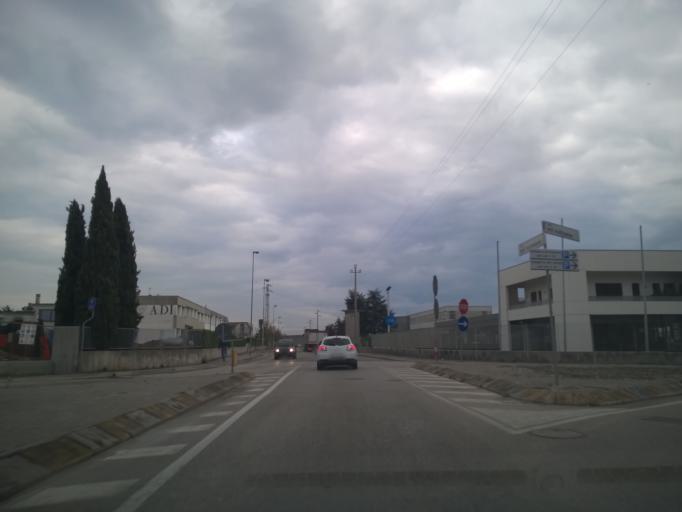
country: IT
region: Veneto
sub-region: Provincia di Vicenza
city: Thiene
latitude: 45.6832
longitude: 11.4678
